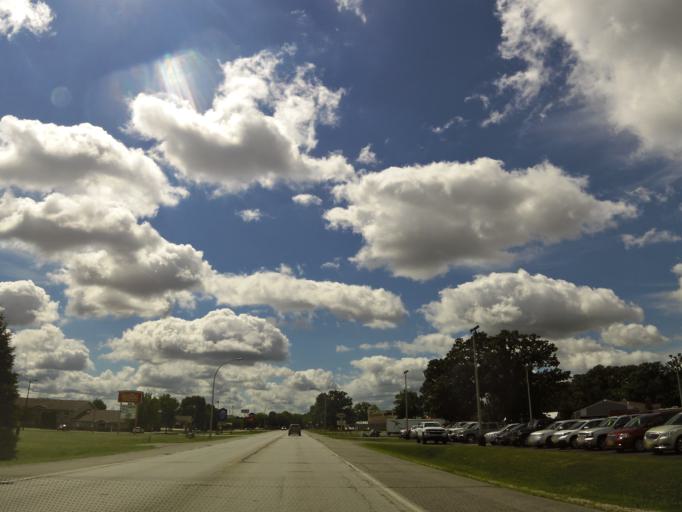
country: US
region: Minnesota
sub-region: Fillmore County
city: Spring Valley
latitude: 43.6988
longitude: -92.3992
